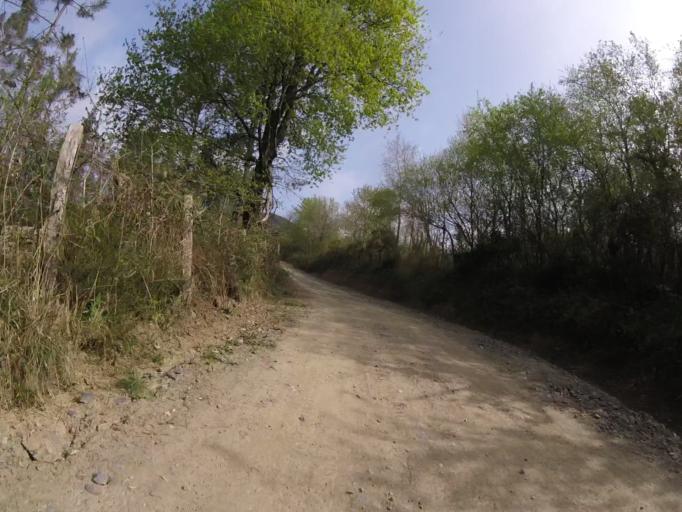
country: ES
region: Basque Country
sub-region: Provincia de Guipuzcoa
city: Zizurkil
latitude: 43.2398
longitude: -2.0786
